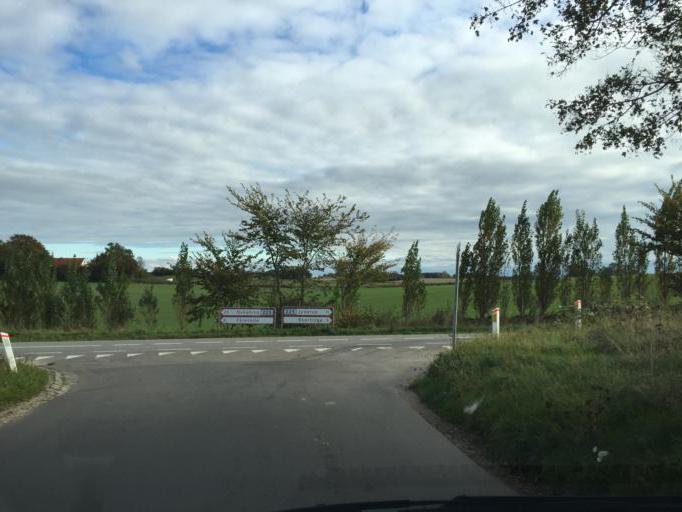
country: DK
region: Zealand
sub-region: Odsherred Kommune
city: Horve
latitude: 55.7517
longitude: 11.3742
